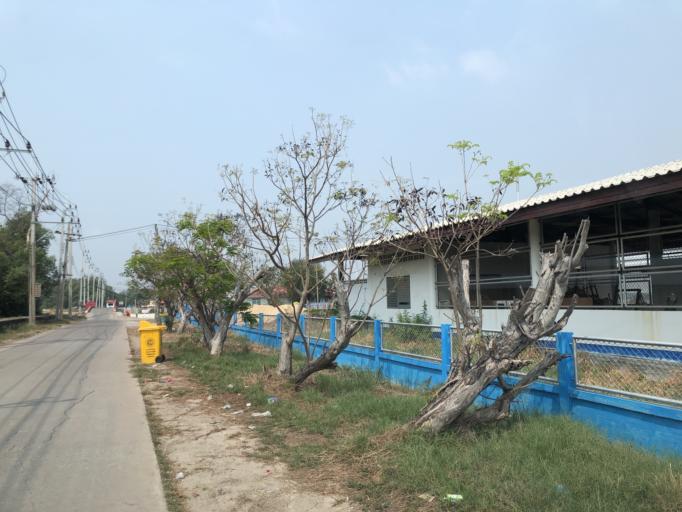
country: TH
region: Samut Prakan
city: Bang Bo
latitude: 13.5174
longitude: 100.8212
